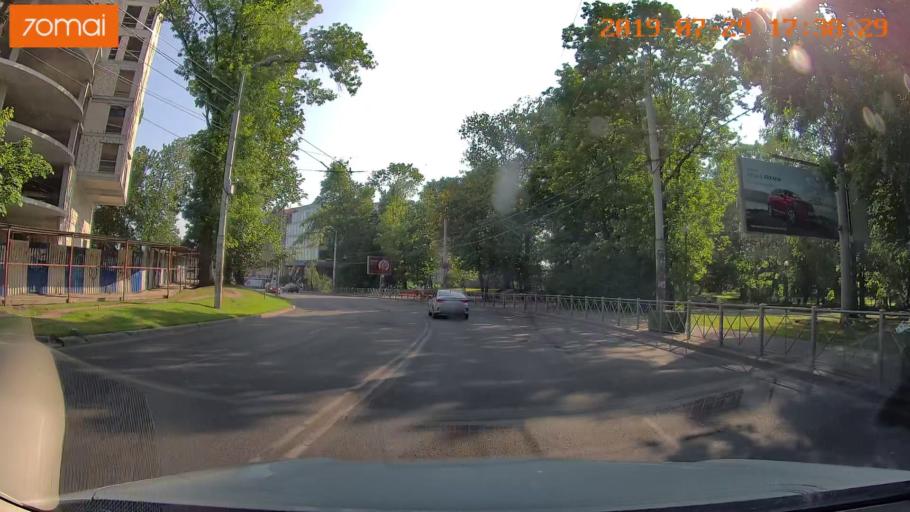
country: RU
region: Kaliningrad
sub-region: Gorod Kaliningrad
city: Kaliningrad
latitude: 54.7229
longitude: 20.5076
